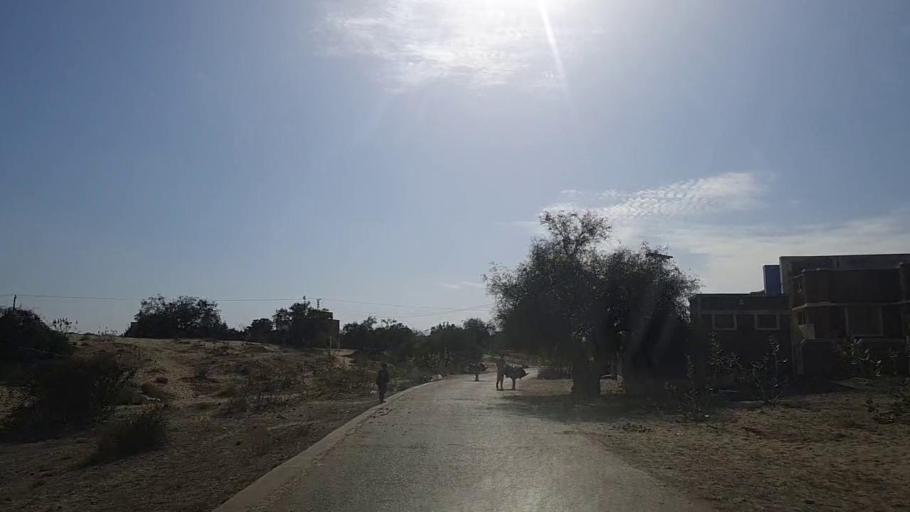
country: PK
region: Sindh
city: Naukot
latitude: 24.8418
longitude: 69.5417
